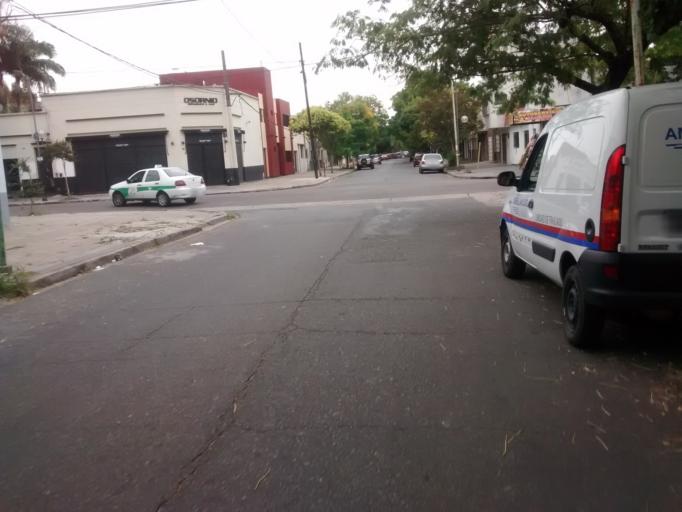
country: AR
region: Buenos Aires
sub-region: Partido de La Plata
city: La Plata
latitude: -34.9379
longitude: -57.9418
